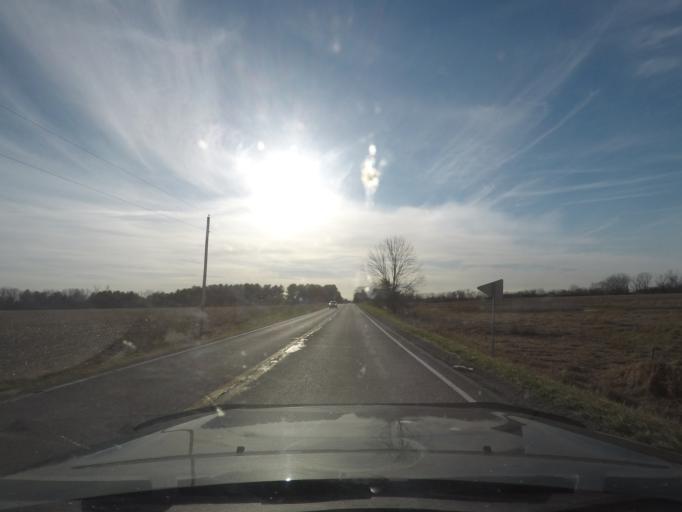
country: US
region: Indiana
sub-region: Saint Joseph County
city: North Liberty
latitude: 41.4484
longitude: -86.3886
